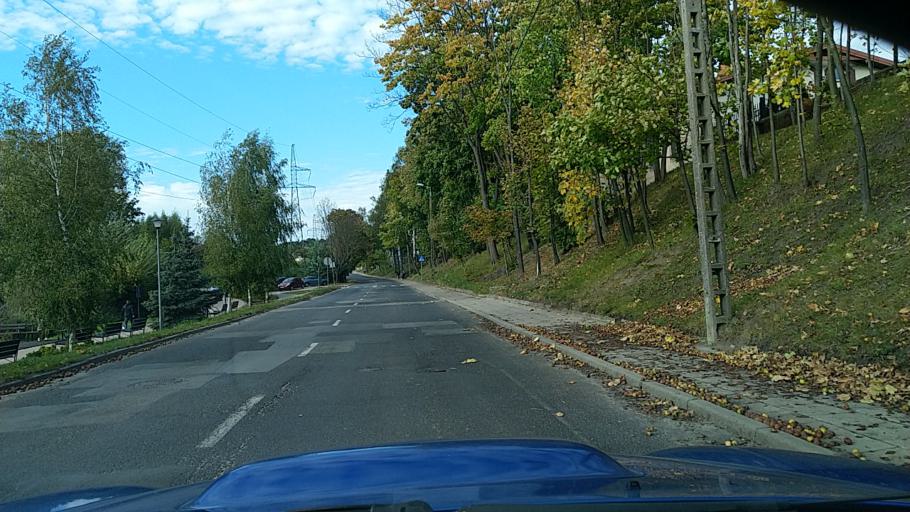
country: PL
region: Warmian-Masurian Voivodeship
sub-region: Olsztyn
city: Kortowo
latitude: 53.7794
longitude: 20.4650
